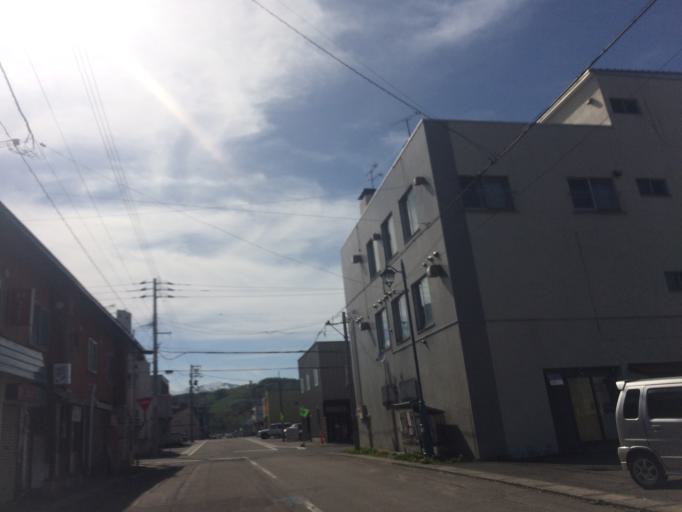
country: JP
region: Hokkaido
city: Niseko Town
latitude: 42.9024
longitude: 140.7509
